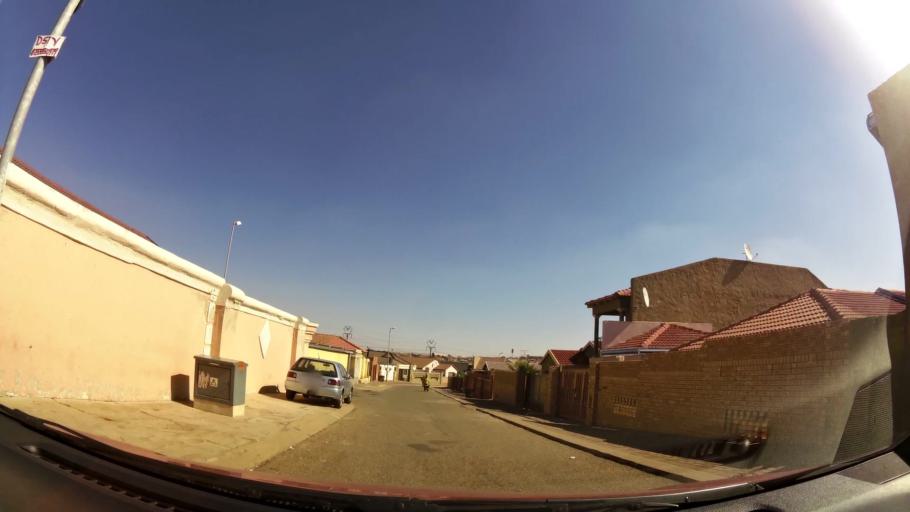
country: ZA
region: Gauteng
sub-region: City of Johannesburg Metropolitan Municipality
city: Soweto
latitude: -26.2357
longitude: 27.8214
